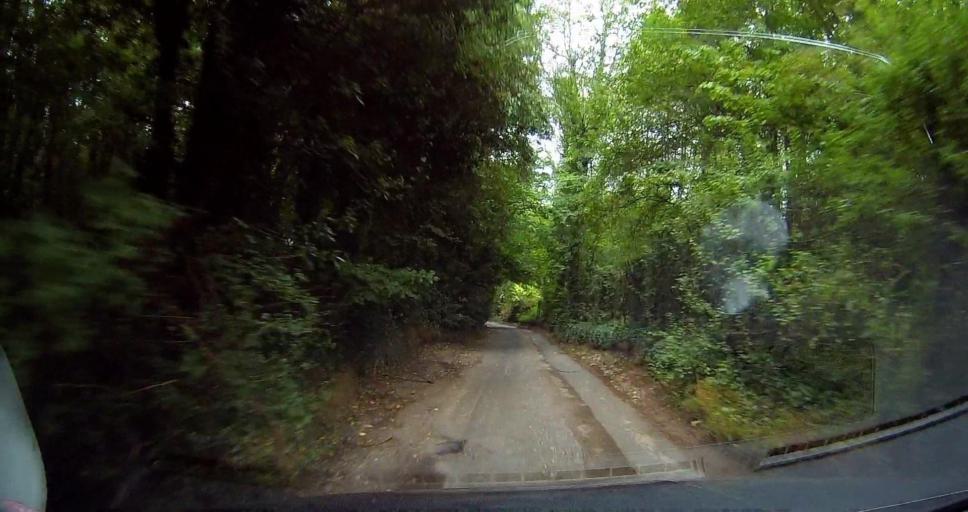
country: GB
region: England
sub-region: Kent
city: Longfield
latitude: 51.3618
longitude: 0.2814
